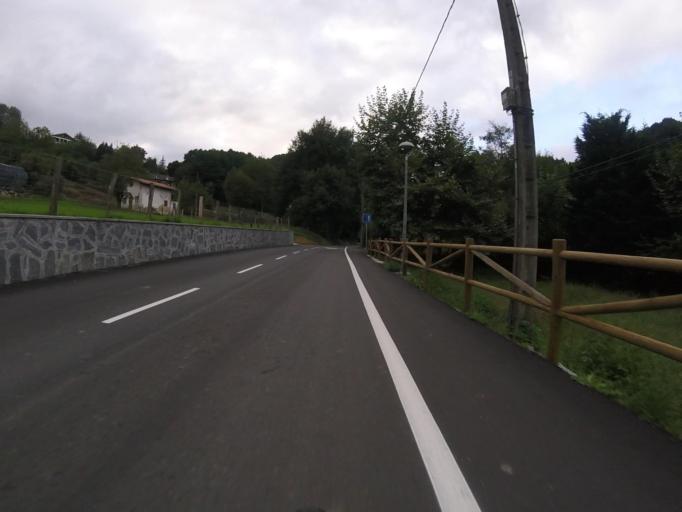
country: ES
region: Basque Country
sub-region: Provincia de Guipuzcoa
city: Errenteria
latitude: 43.2839
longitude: -1.8543
